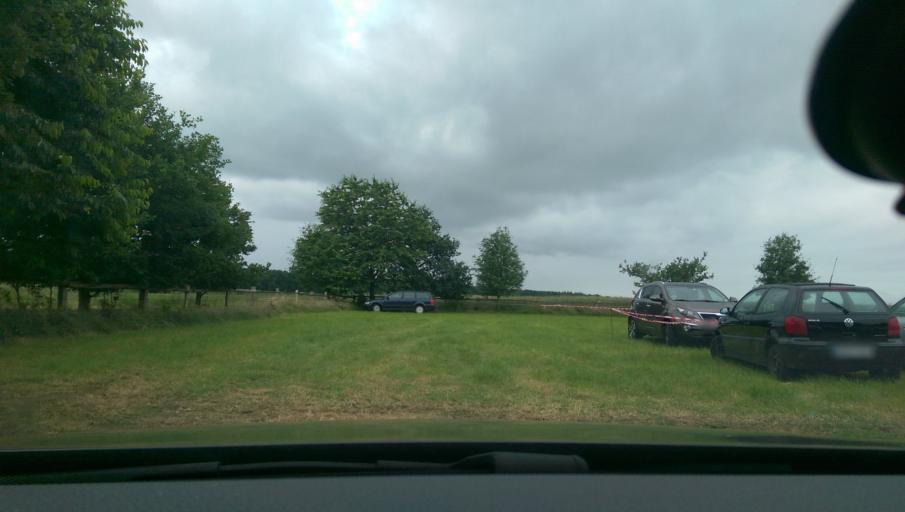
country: DE
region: Lower Saxony
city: Horstedt
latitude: 53.1743
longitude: 9.2324
